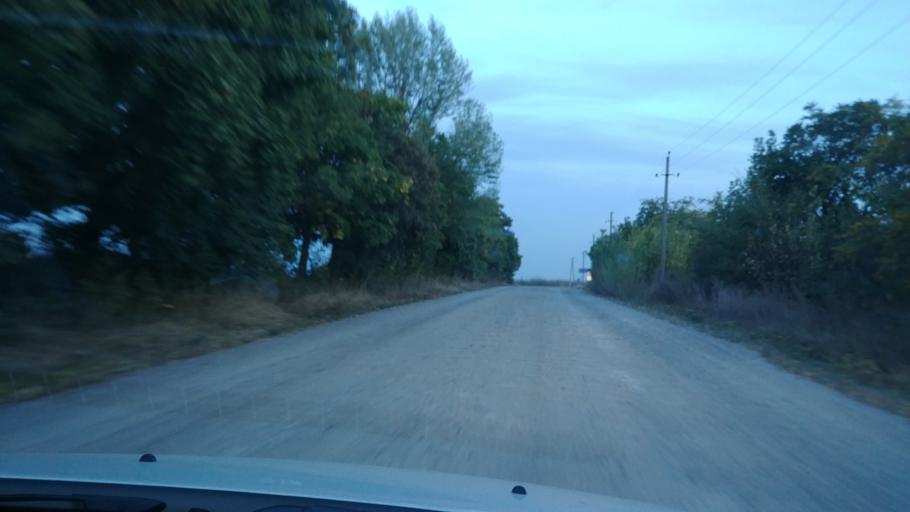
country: MD
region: Rezina
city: Saharna
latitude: 47.6699
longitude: 28.9429
